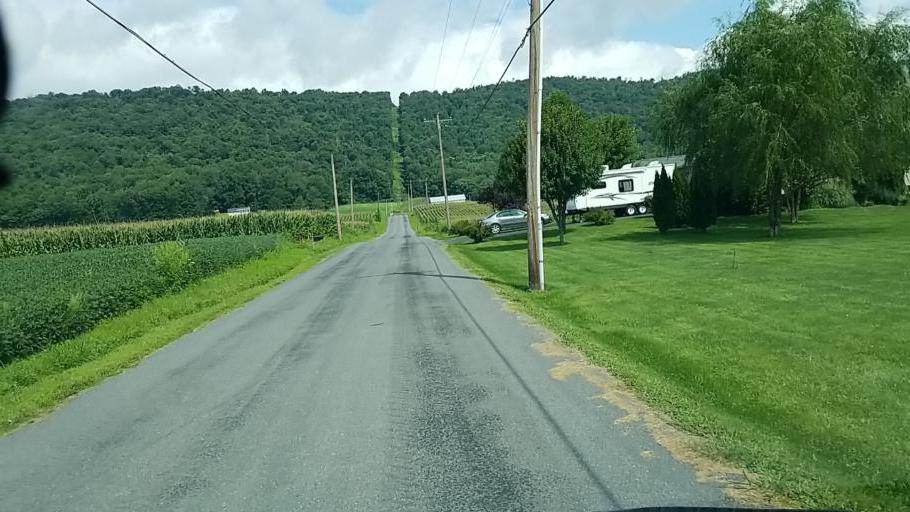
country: US
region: Pennsylvania
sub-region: Dauphin County
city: Millersburg
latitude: 40.5764
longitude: -76.9319
